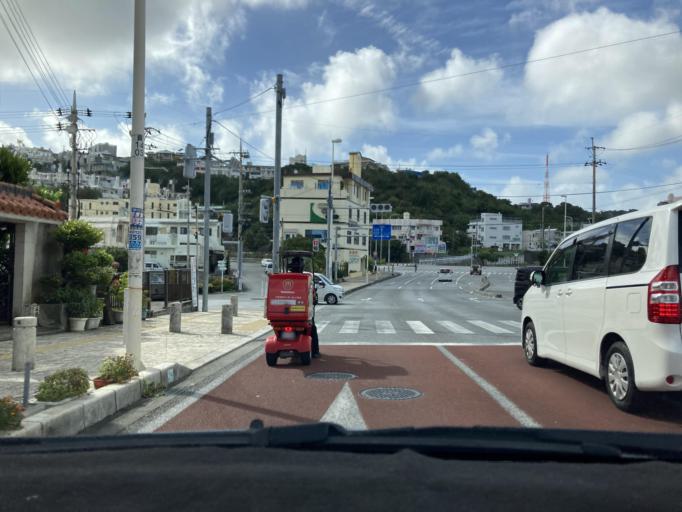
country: JP
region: Okinawa
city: Tomigusuku
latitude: 26.1949
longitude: 127.6954
